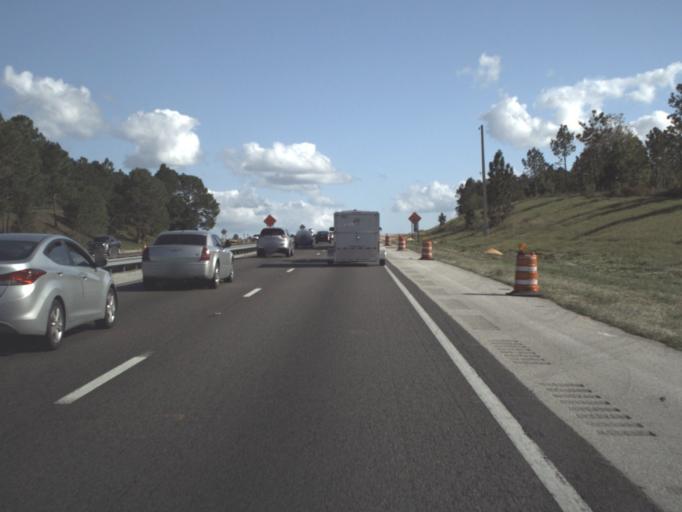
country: US
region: Florida
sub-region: Lake County
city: Minneola
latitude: 28.6047
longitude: -81.7237
